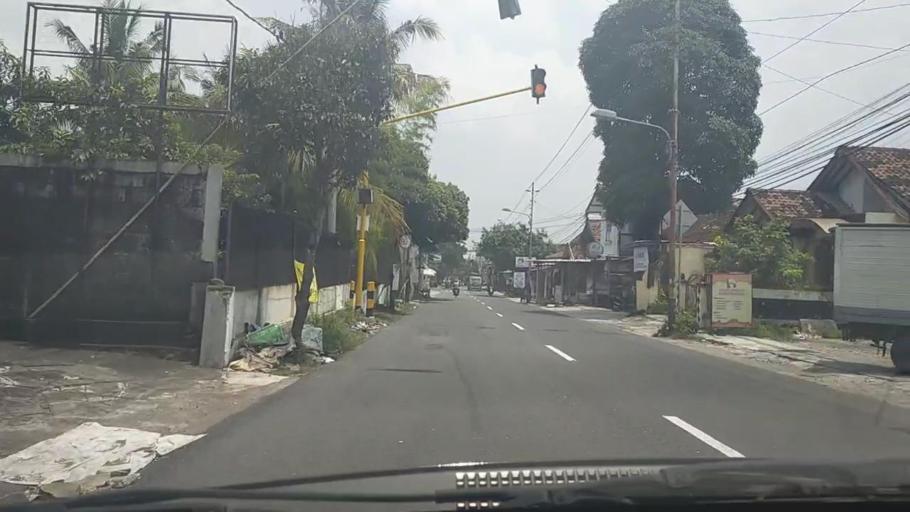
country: ID
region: Daerah Istimewa Yogyakarta
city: Melati
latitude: -7.7085
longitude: 110.3875
